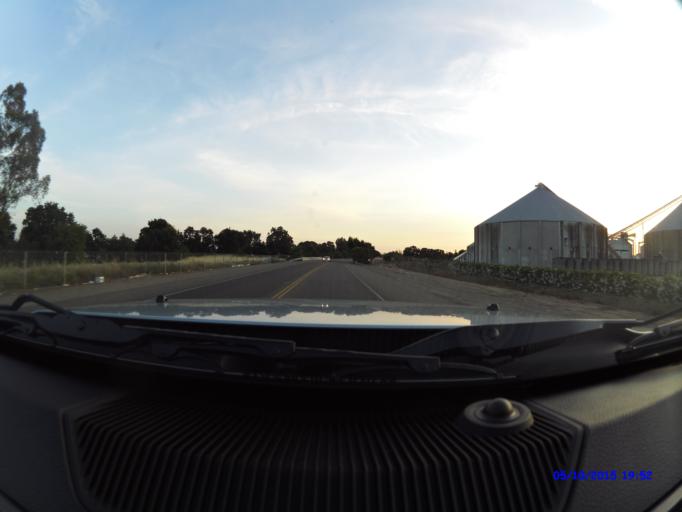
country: US
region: California
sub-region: San Joaquin County
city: Kennedy
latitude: 37.9478
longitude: -121.2494
